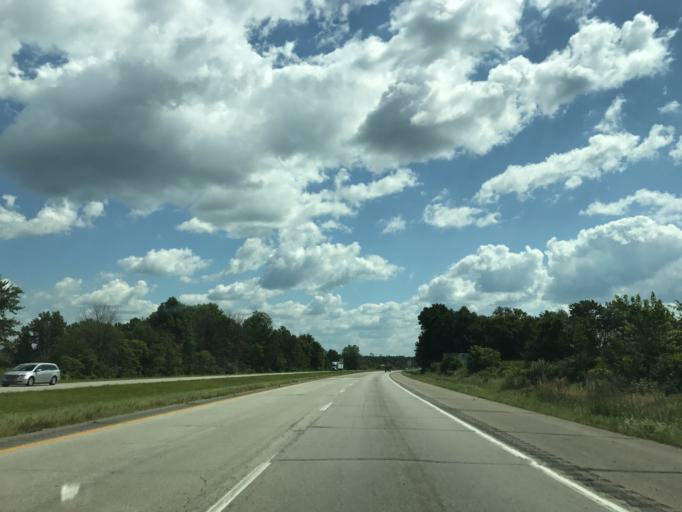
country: US
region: Indiana
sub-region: Marshall County
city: Plymouth
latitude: 41.3645
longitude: -86.3845
